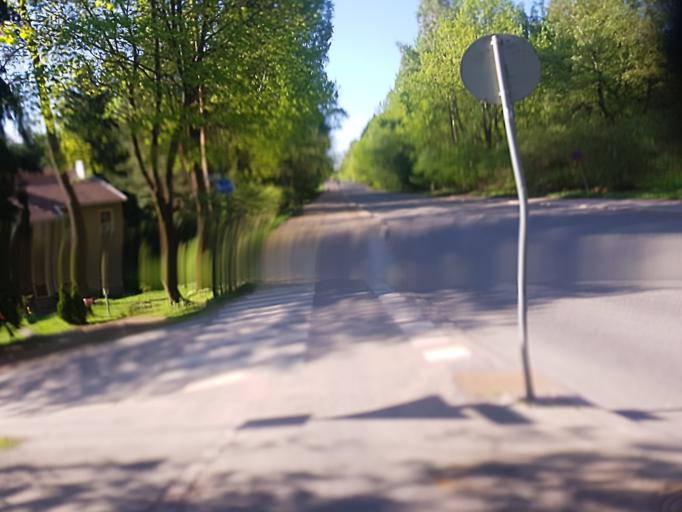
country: FI
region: Uusimaa
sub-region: Helsinki
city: Helsinki
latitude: 60.2265
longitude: 24.9341
